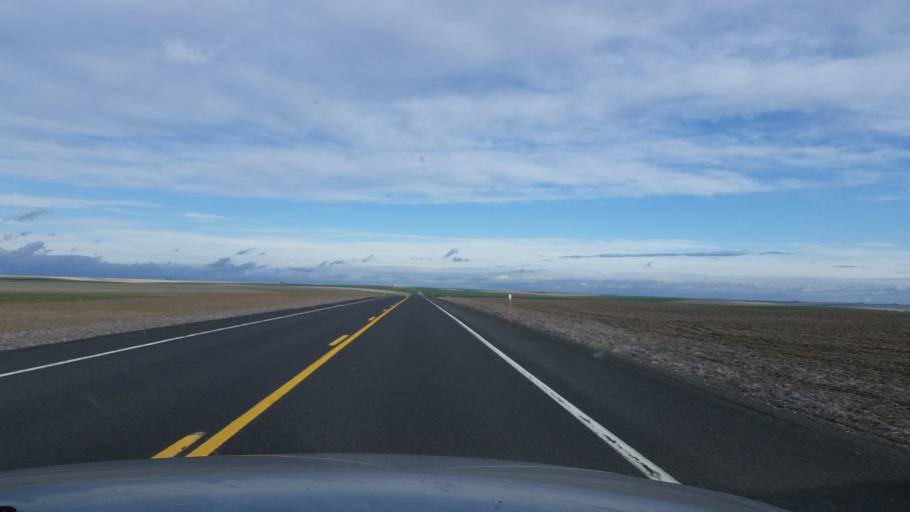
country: US
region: Washington
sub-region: Adams County
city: Ritzville
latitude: 47.3902
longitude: -118.4123
